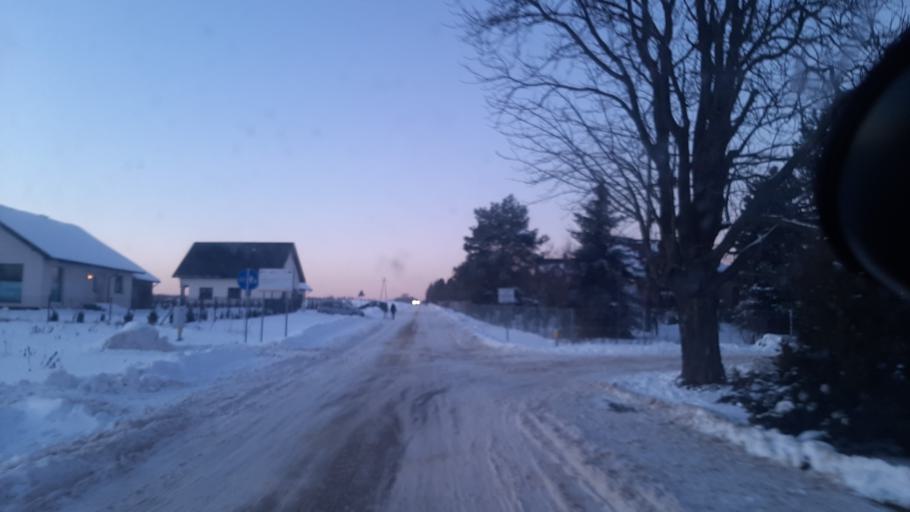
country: PL
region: Lublin Voivodeship
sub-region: Powiat lubelski
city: Niemce
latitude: 51.3635
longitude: 22.5288
